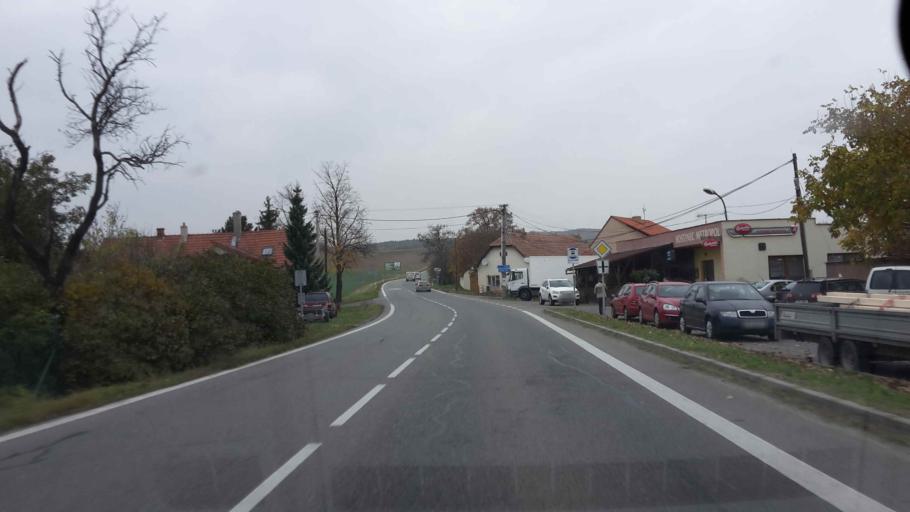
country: CZ
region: South Moravian
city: Damborice
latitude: 49.0514
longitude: 16.9534
